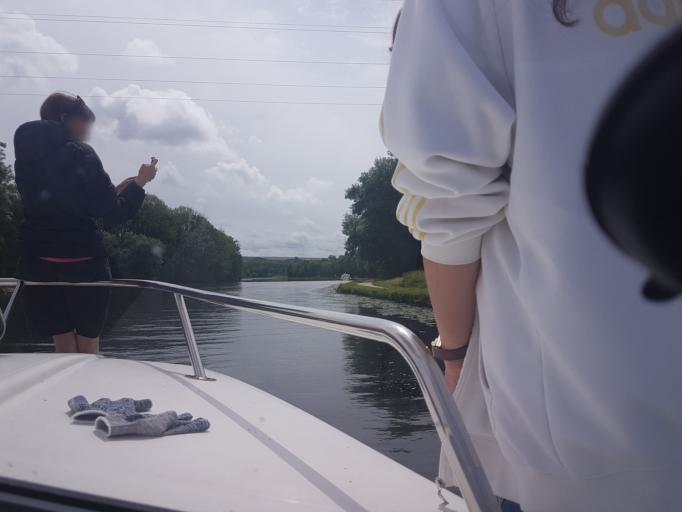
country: FR
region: Bourgogne
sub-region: Departement de l'Yonne
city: Augy
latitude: 47.7825
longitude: 3.5991
